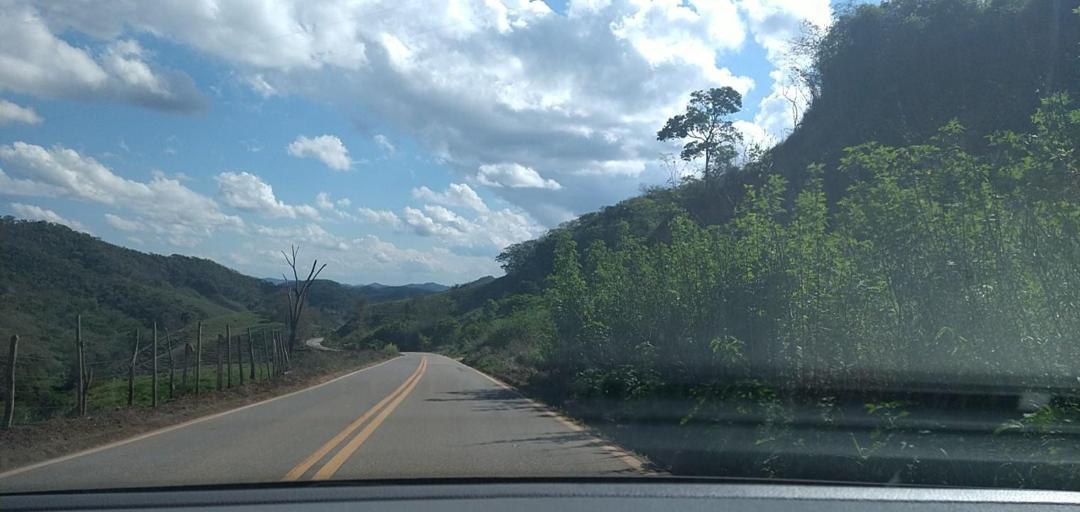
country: BR
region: Minas Gerais
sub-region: Alvinopolis
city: Alvinopolis
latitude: -20.0463
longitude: -43.0349
